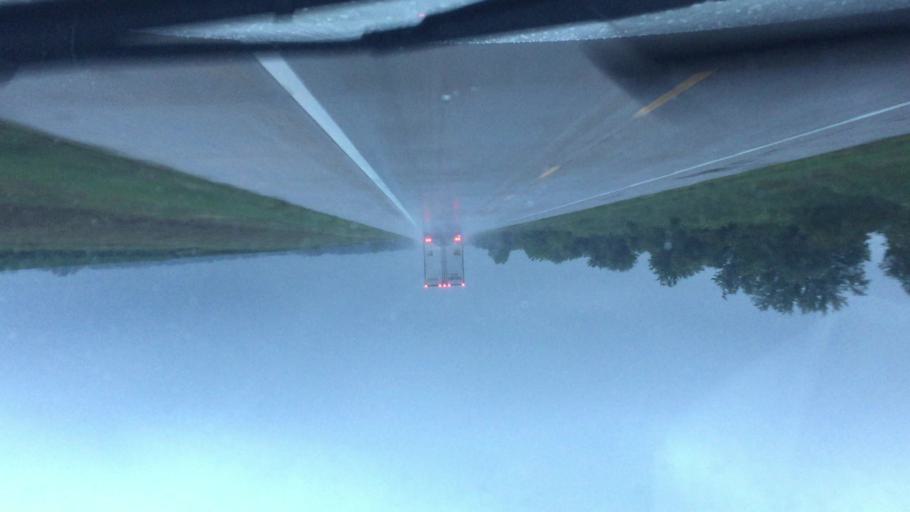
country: US
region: Kansas
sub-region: Neosho County
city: Chanute
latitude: 37.5706
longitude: -95.4709
